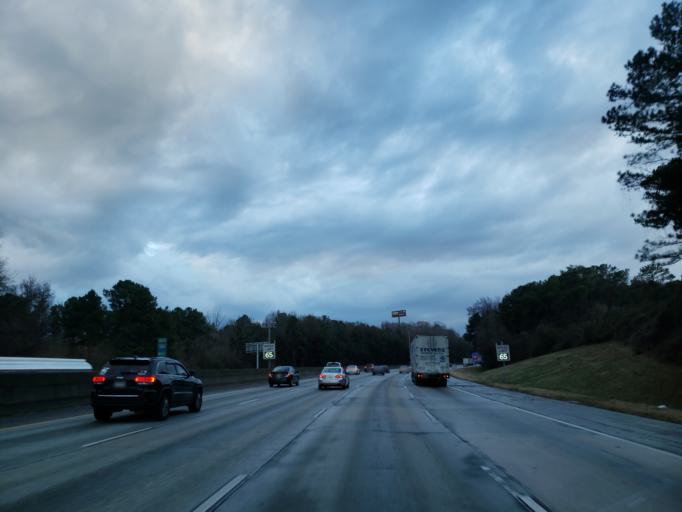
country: US
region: Georgia
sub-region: Cobb County
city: Vinings
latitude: 33.8052
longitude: -84.4945
